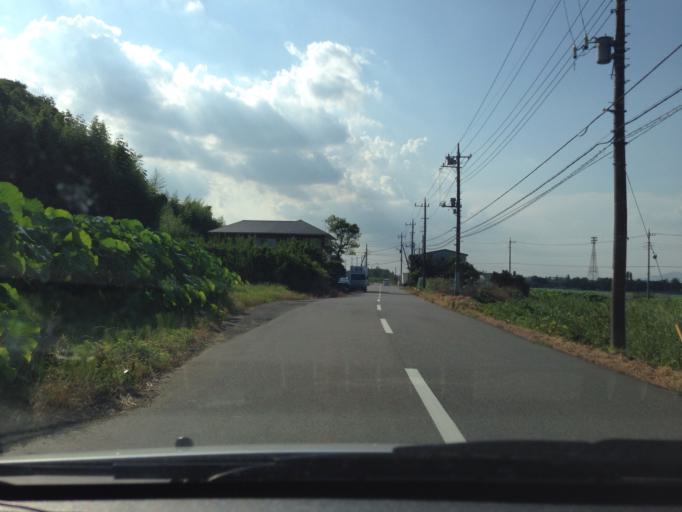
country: JP
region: Ibaraki
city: Ami
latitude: 36.0408
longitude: 140.2306
